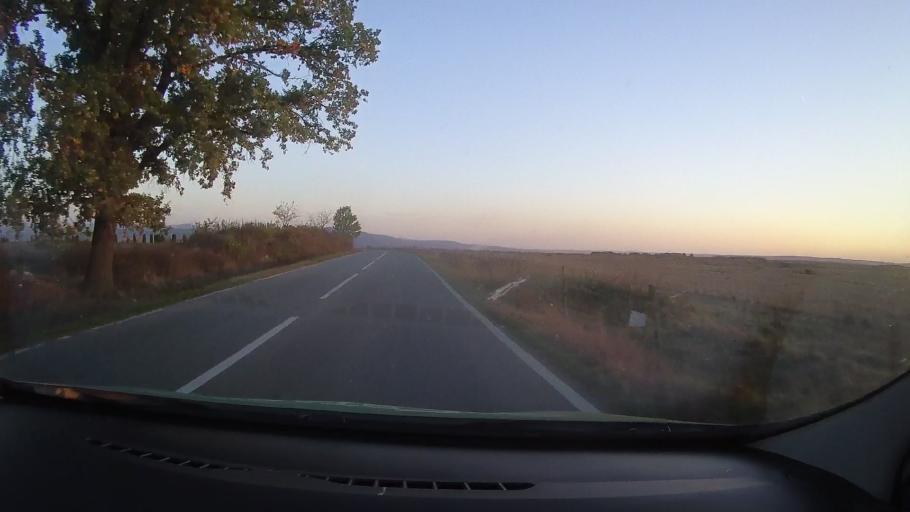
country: RO
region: Timis
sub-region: Comuna Manastiur
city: Manastiur
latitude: 45.8198
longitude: 22.0705
